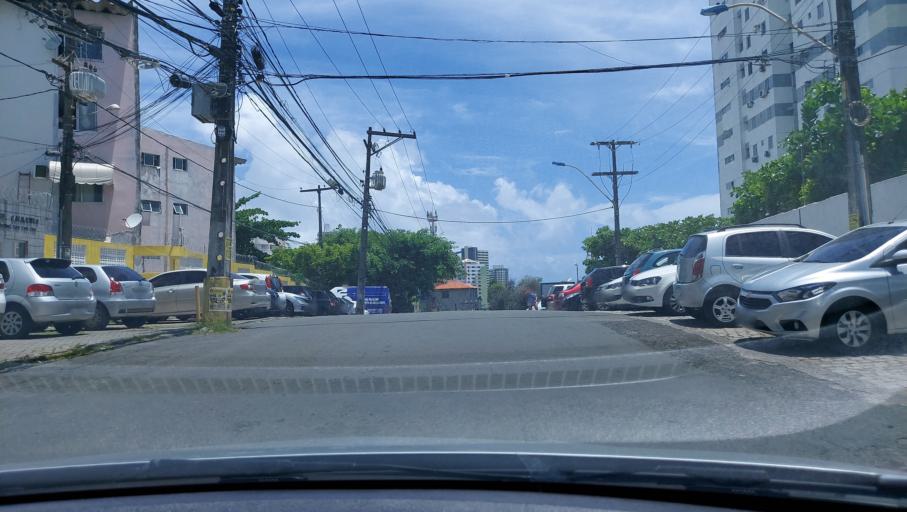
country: BR
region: Bahia
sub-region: Salvador
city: Salvador
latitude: -12.9865
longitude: -38.4739
